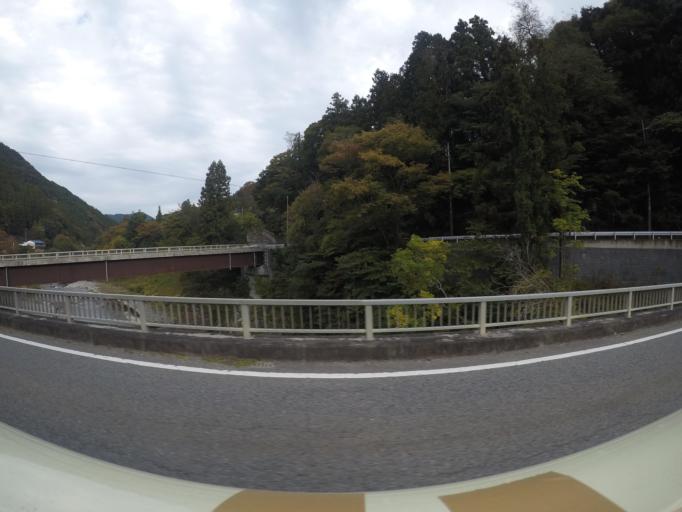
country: JP
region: Gunma
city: Tomioka
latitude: 36.1044
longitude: 138.8891
